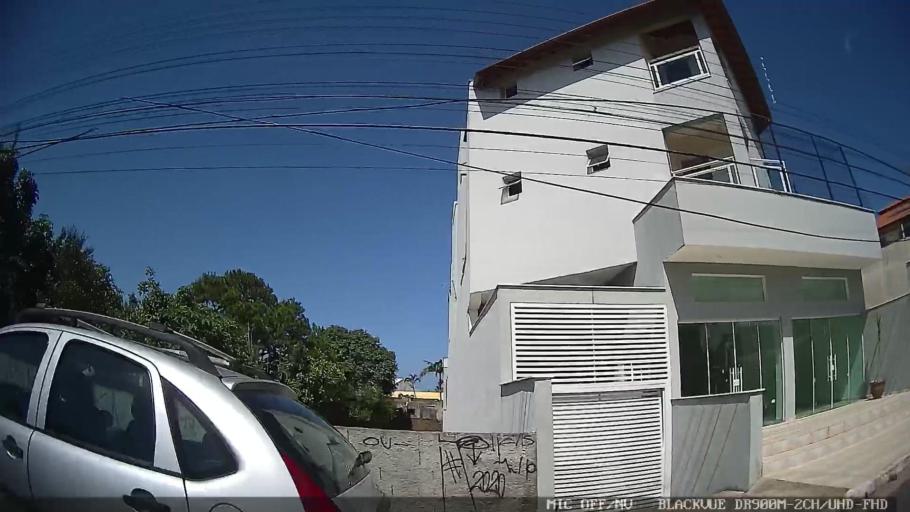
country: BR
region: Sao Paulo
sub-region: Peruibe
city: Peruibe
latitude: -24.3280
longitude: -47.0030
